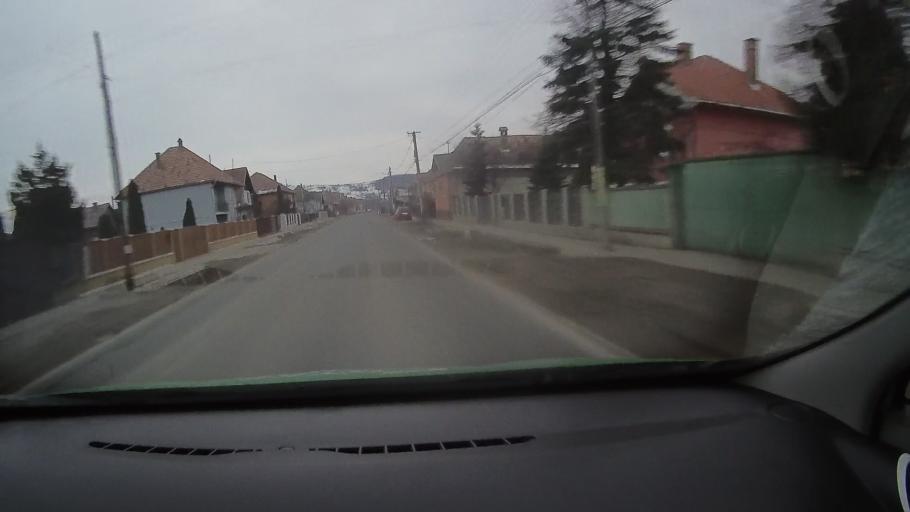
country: RO
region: Harghita
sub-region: Comuna Feliceni
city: Feliceni
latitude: 46.2716
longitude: 25.2761
